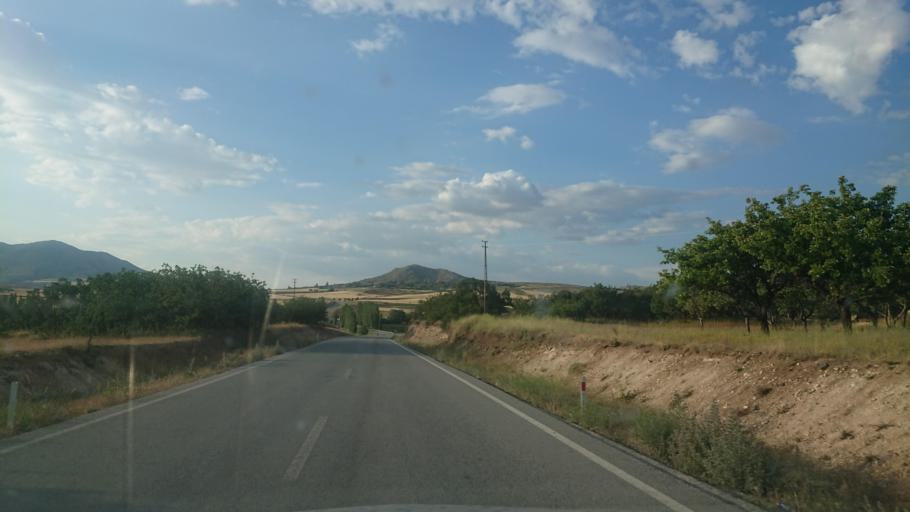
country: TR
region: Aksaray
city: Balci
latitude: 38.5685
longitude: 34.1056
